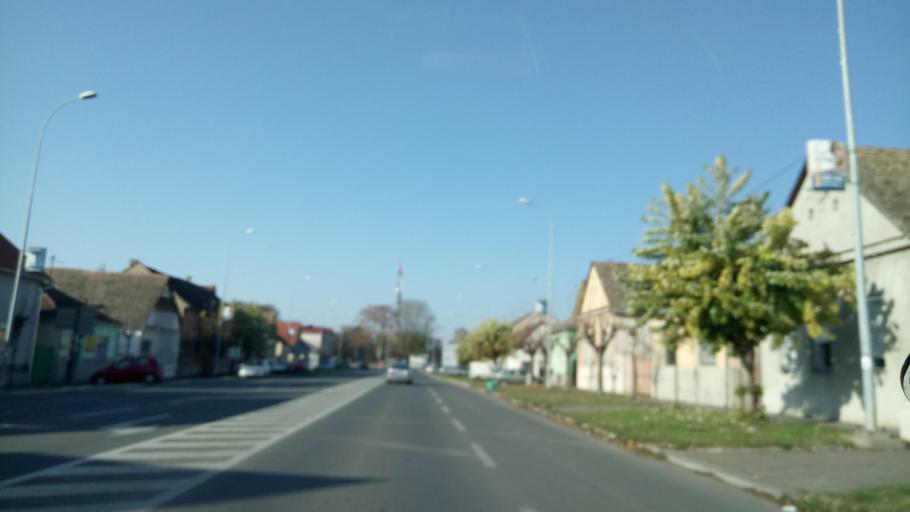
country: RS
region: Autonomna Pokrajina Vojvodina
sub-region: Sremski Okrug
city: Ingija
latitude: 45.0512
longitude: 20.0771
